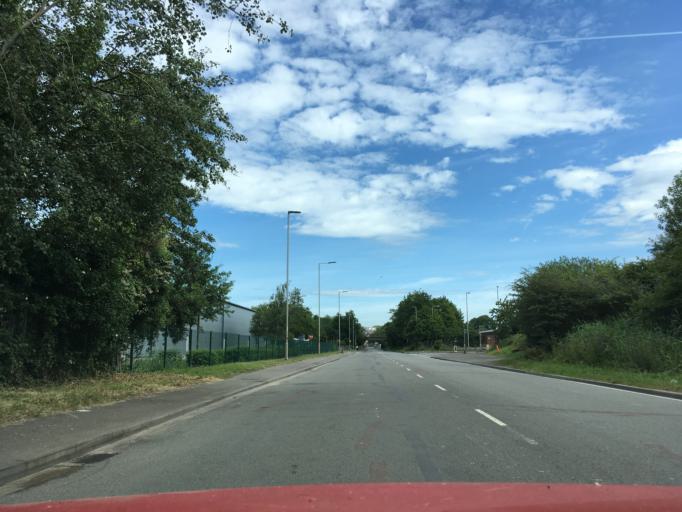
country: GB
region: Wales
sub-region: Newport
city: Nash
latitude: 51.5713
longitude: -2.9694
